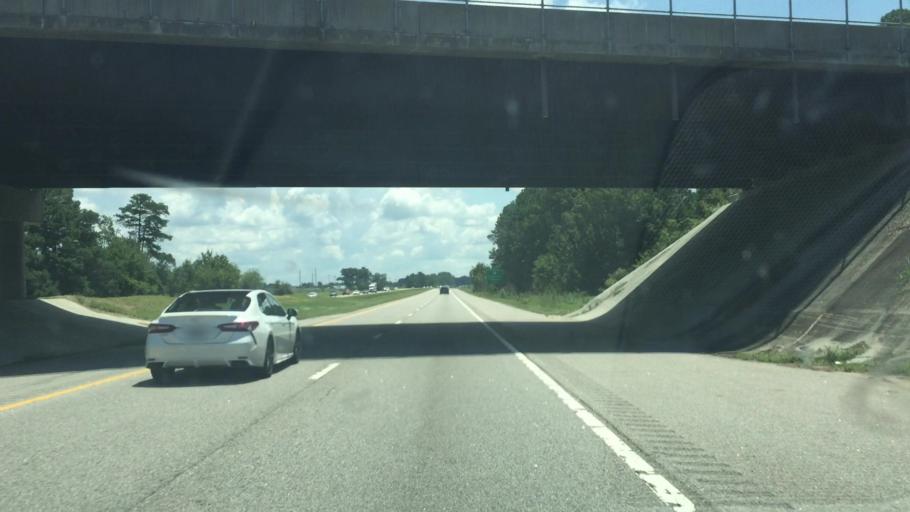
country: US
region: North Carolina
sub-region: Robeson County
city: Lumberton
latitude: 34.5901
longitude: -79.0689
